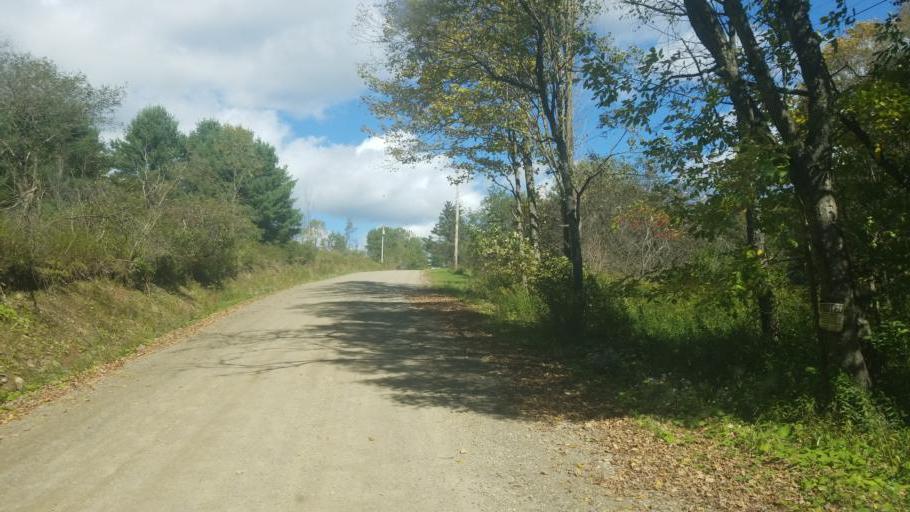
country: US
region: New York
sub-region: Allegany County
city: Cuba
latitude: 42.1732
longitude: -78.3318
